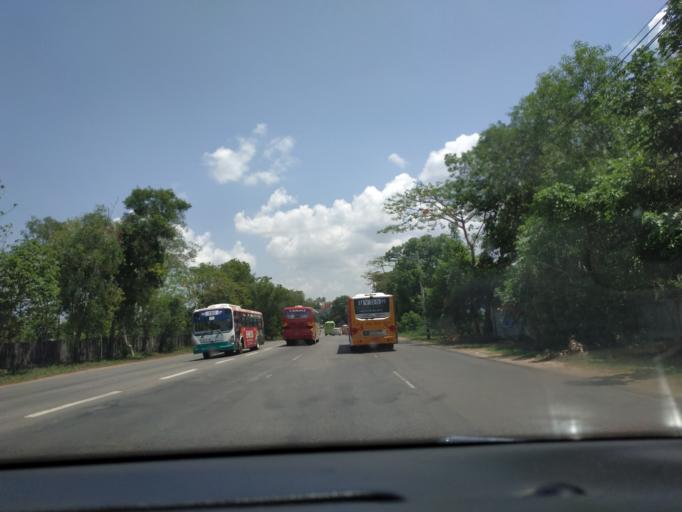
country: MM
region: Yangon
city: Yangon
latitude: 17.0026
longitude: 96.1294
